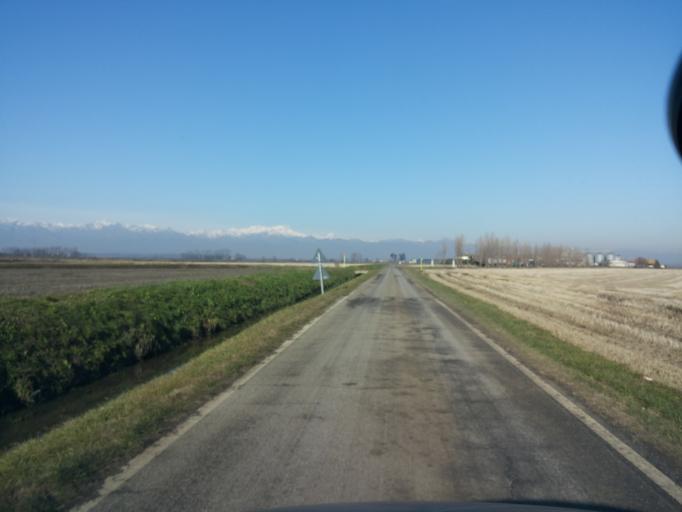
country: IT
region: Piedmont
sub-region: Provincia di Vercelli
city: San Germano Vercellese
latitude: 45.3654
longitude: 8.2421
